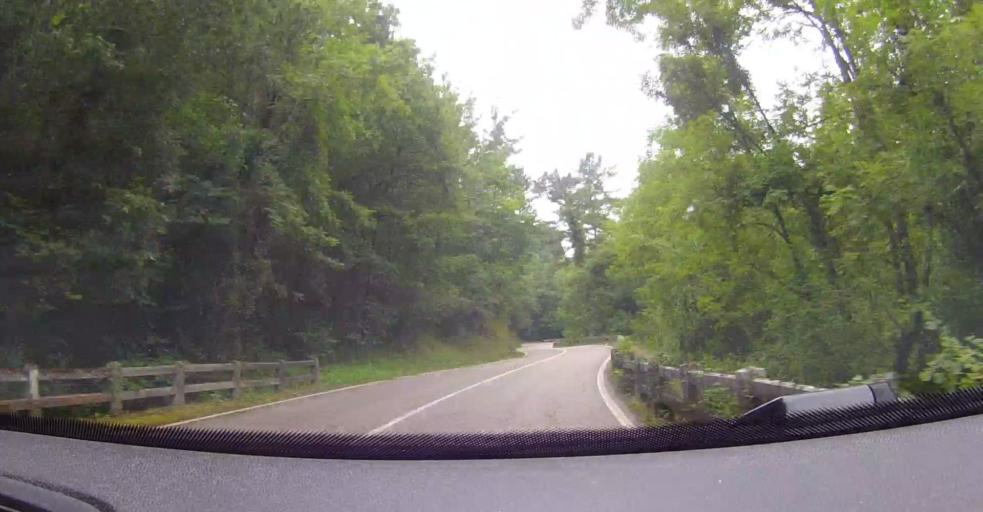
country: ES
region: Basque Country
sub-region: Bizkaia
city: Balmaseda
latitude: 43.2432
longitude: -3.2768
